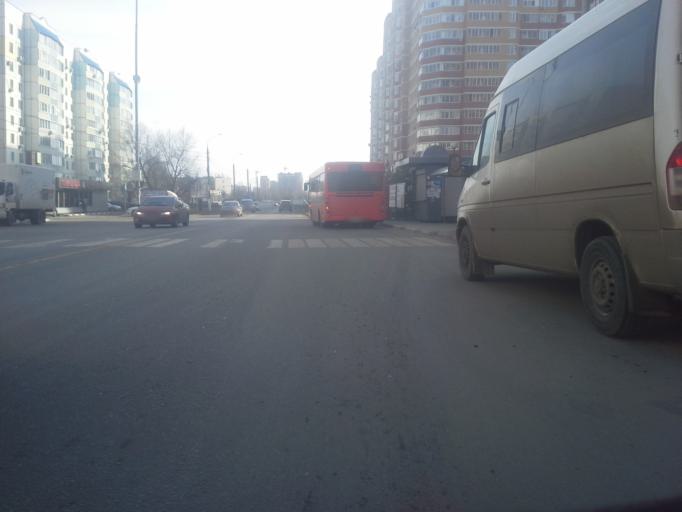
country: RU
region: Moskovskaya
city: Shcherbinka
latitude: 55.4688
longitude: 37.5454
